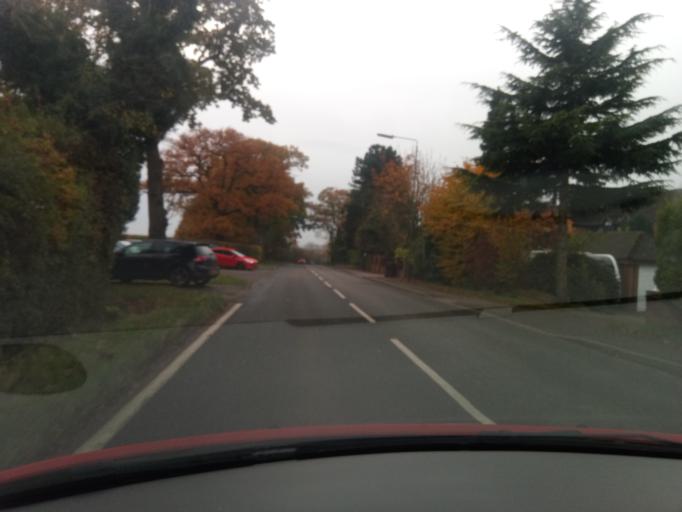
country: GB
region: England
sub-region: Derbyshire
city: Little Eaton
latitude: 52.9439
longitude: -1.4180
